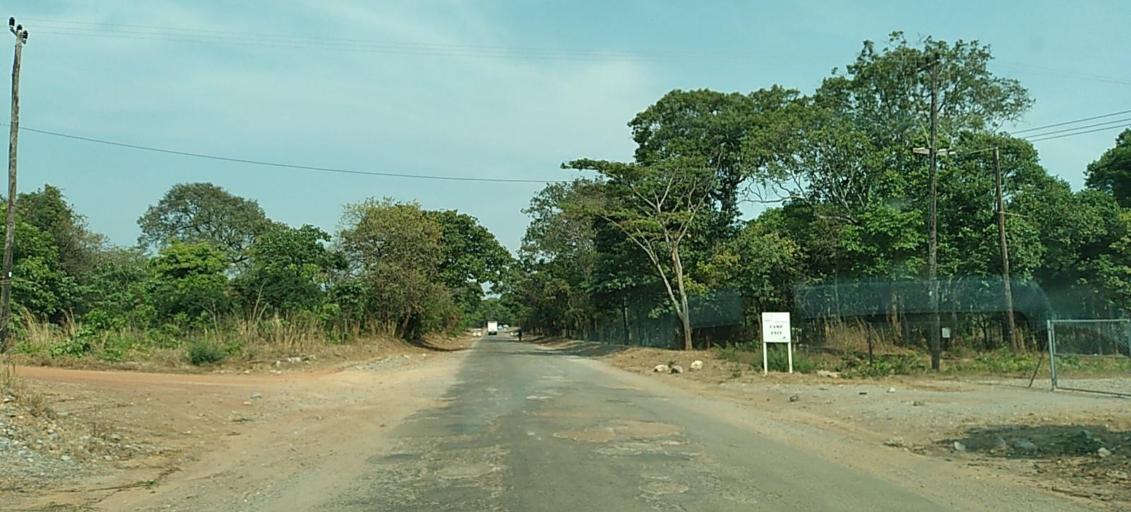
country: ZM
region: Copperbelt
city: Chililabombwe
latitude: -12.3035
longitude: 27.7809
